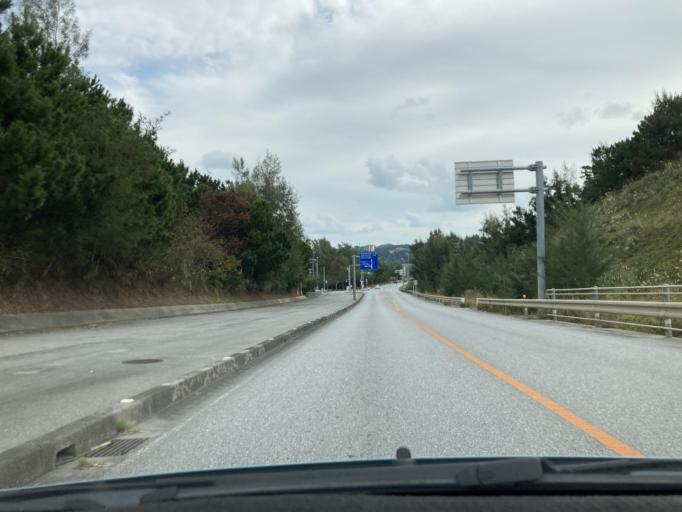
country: JP
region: Okinawa
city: Ishikawa
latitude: 26.5039
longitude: 127.8780
